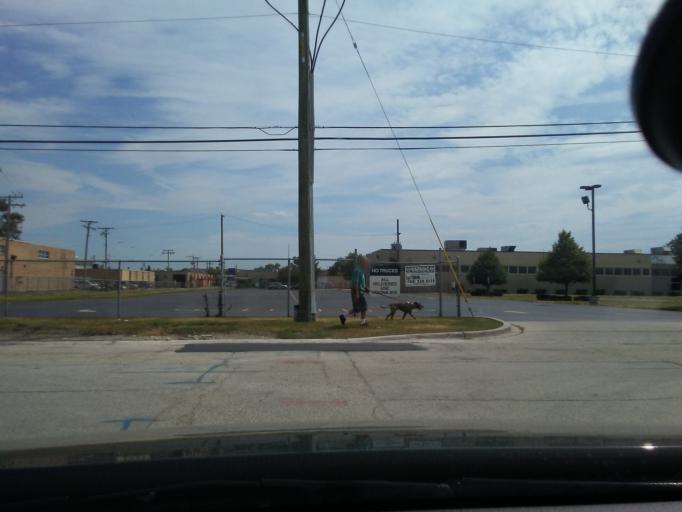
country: US
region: Illinois
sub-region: Cook County
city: Schiller Park
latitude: 41.9733
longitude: -87.8655
